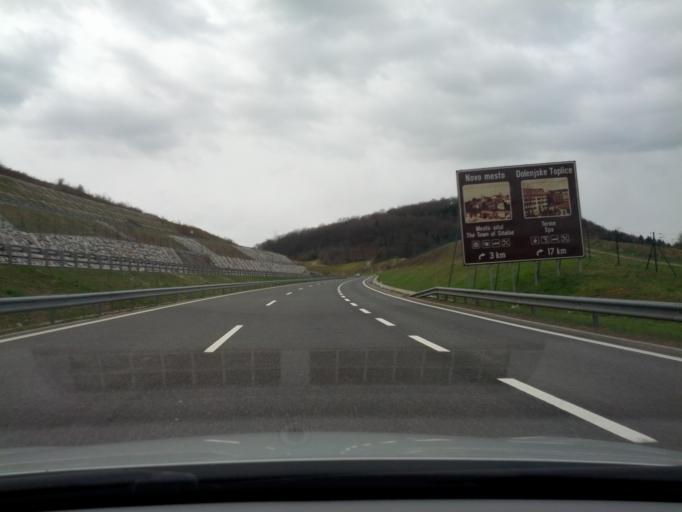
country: SI
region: Mirna Pec
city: Mirna Pec
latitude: 45.8588
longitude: 15.1422
